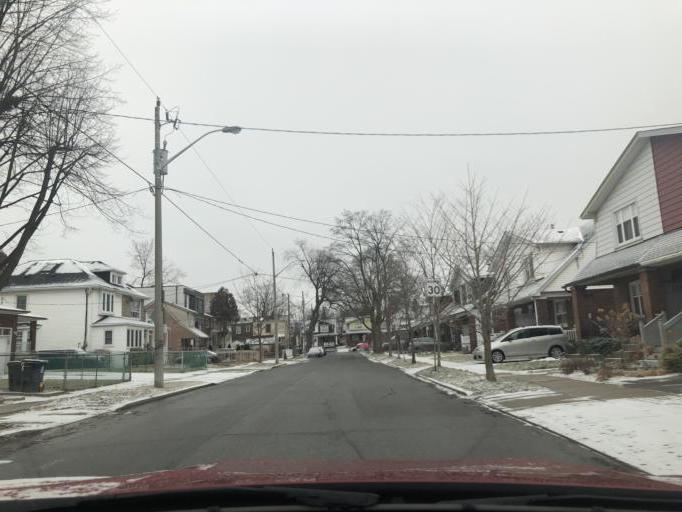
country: CA
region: Ontario
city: Toronto
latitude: 43.6847
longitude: -79.3408
